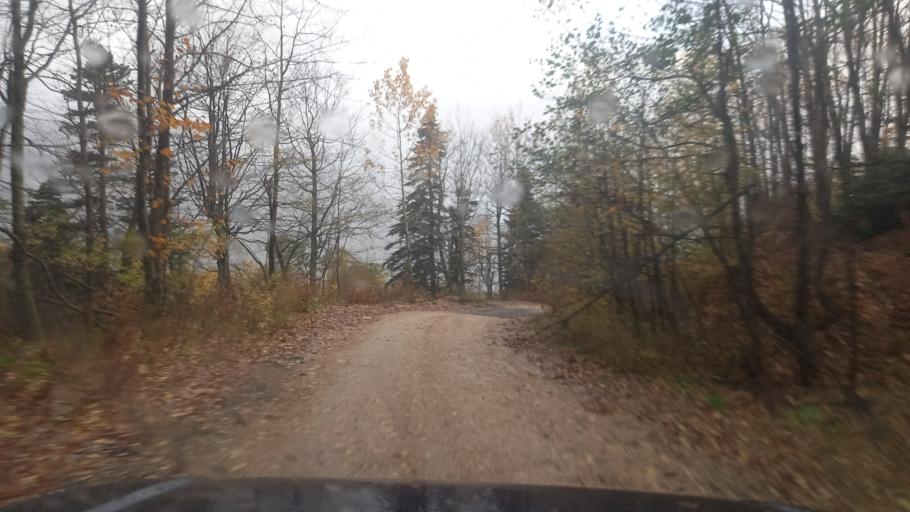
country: RU
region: Krasnodarskiy
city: Neftegorsk
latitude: 44.0134
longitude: 39.8432
